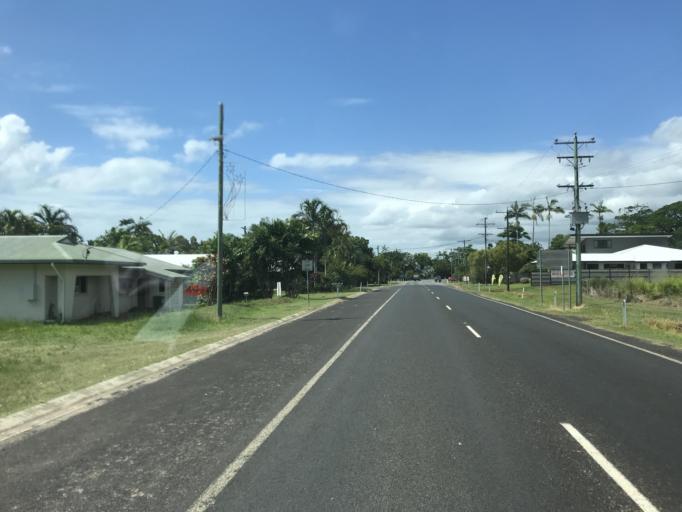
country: AU
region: Queensland
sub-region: Cassowary Coast
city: Innisfail
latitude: -17.8683
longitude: 146.1067
